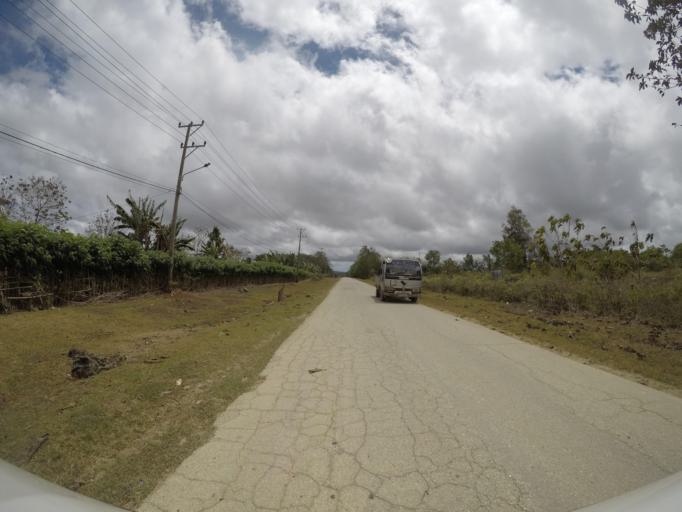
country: TL
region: Lautem
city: Lospalos
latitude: -8.4854
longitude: 126.9926
